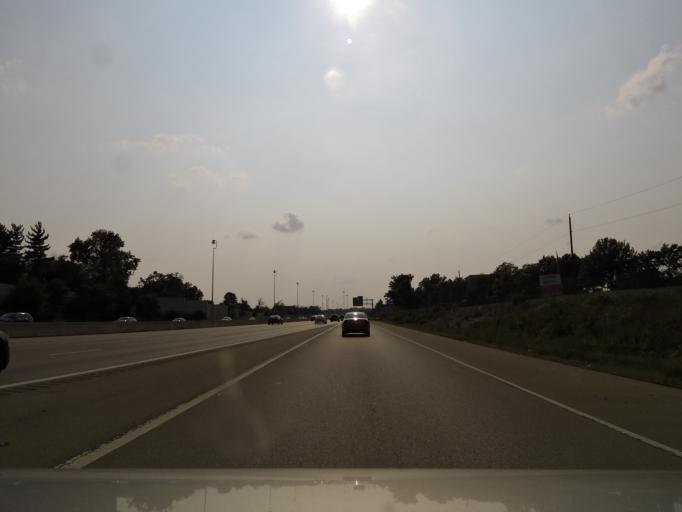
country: US
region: Ohio
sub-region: Hamilton County
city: Springdale
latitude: 39.2954
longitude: -84.4715
